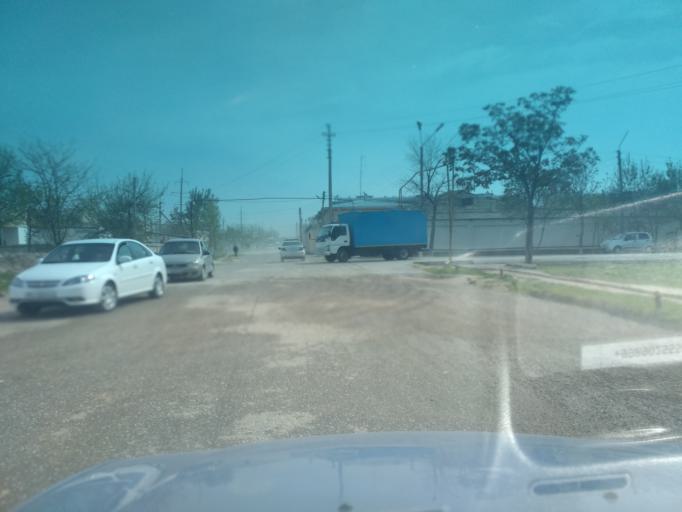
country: UZ
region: Sirdaryo
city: Guliston
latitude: 40.5036
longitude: 68.7683
